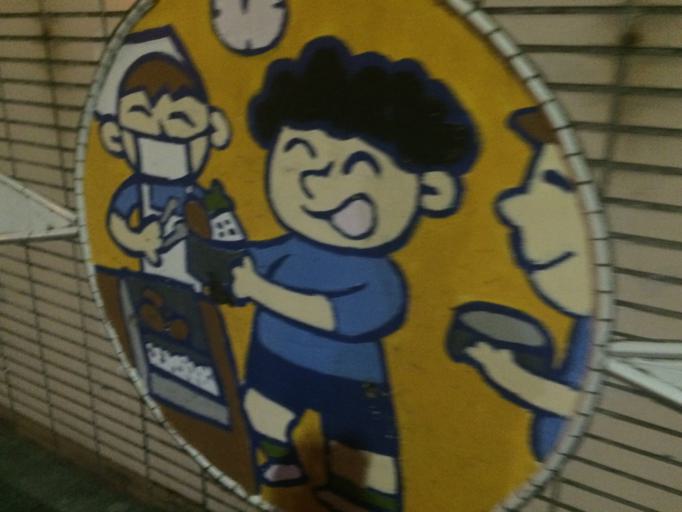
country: TW
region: Taipei
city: Taipei
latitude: 25.0263
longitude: 121.5035
